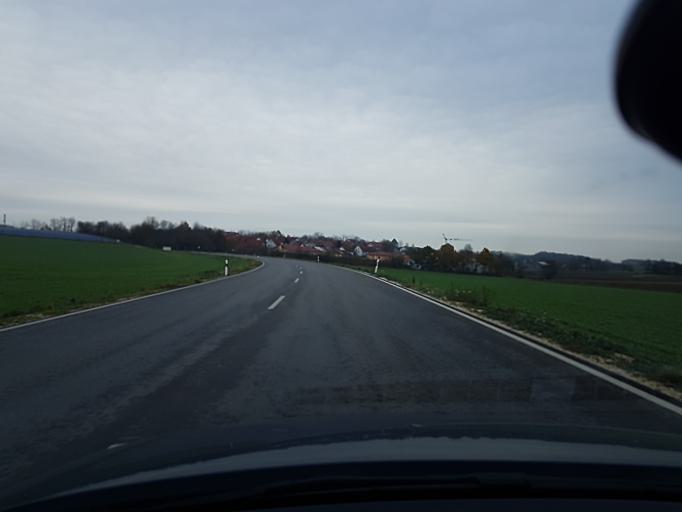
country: DE
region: Bavaria
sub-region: Upper Palatinate
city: Schierling
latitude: 48.8309
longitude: 12.1798
